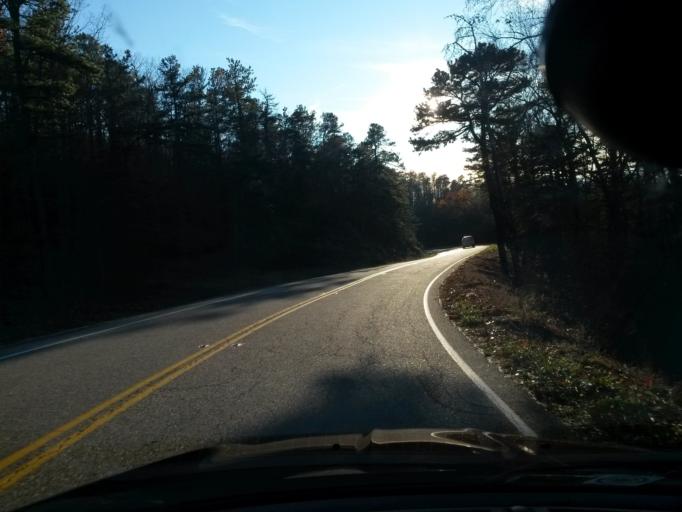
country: US
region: Virginia
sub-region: City of Buena Vista
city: Buena Vista
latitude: 37.7369
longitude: -79.3080
